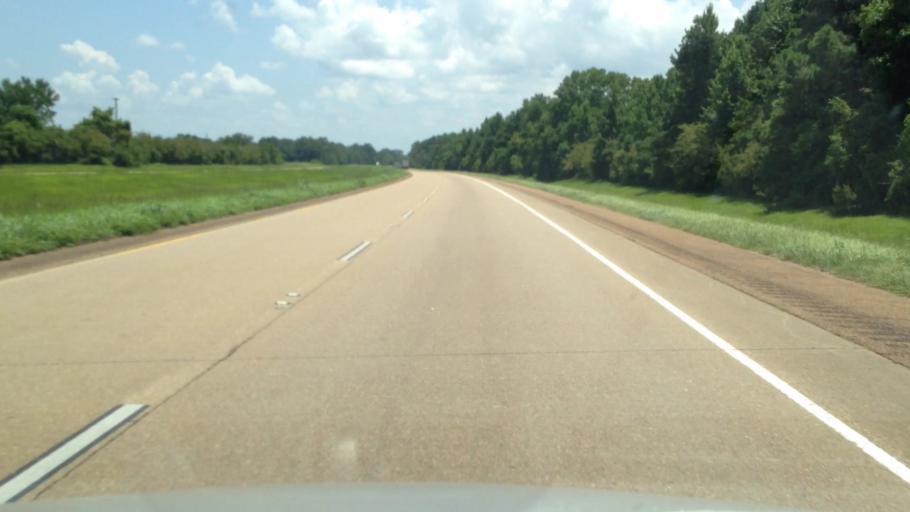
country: US
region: Louisiana
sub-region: Rapides Parish
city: Woodworth
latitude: 31.1398
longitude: -92.4509
